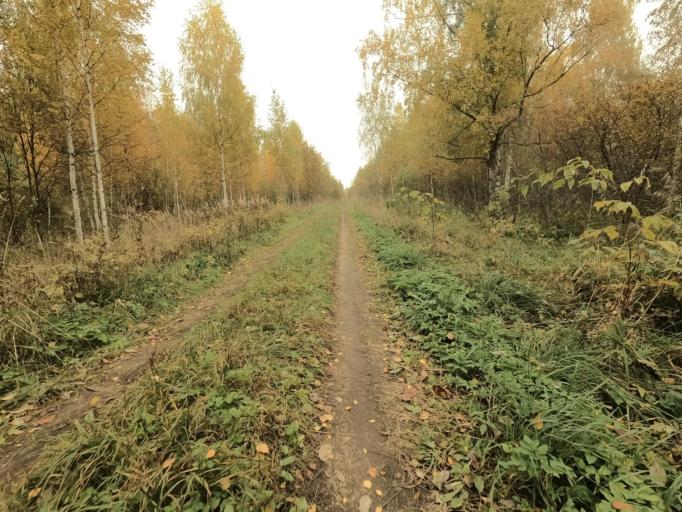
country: RU
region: Novgorod
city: Pankovka
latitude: 58.8788
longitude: 30.9420
